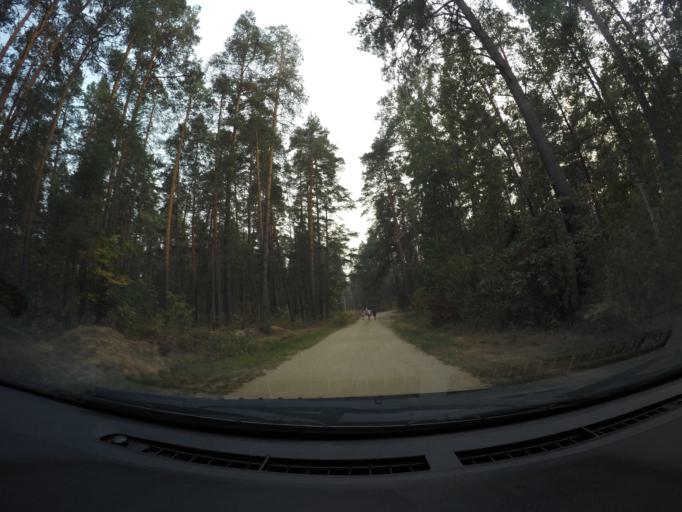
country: RU
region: Moskovskaya
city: Imeni Tsyurupy
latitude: 55.5046
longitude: 38.6929
